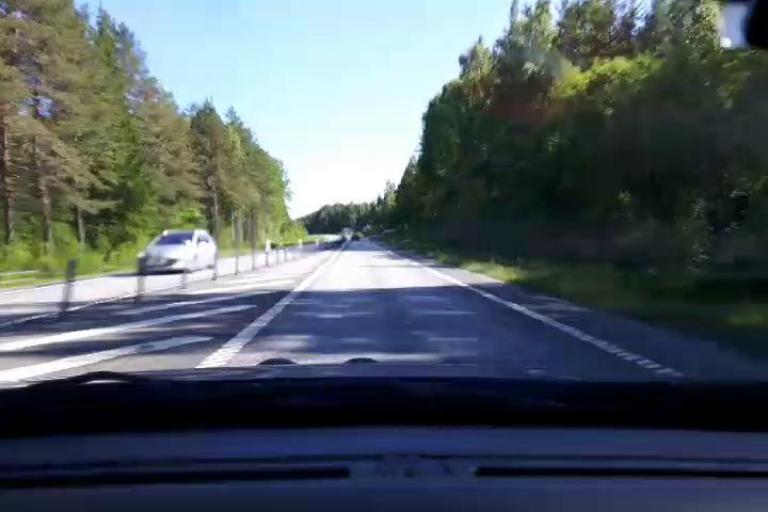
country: SE
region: Gaevleborg
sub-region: Gavle Kommun
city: Norrsundet
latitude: 61.0096
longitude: 16.9830
